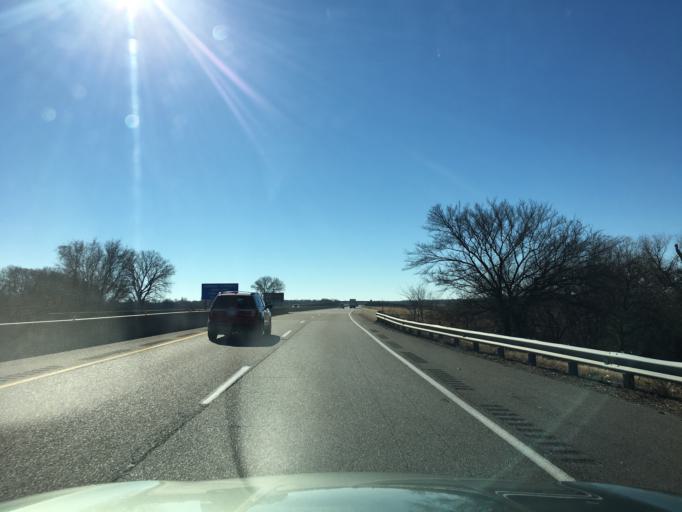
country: US
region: Kansas
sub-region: Sumner County
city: Belle Plaine
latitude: 37.4146
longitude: -97.3215
